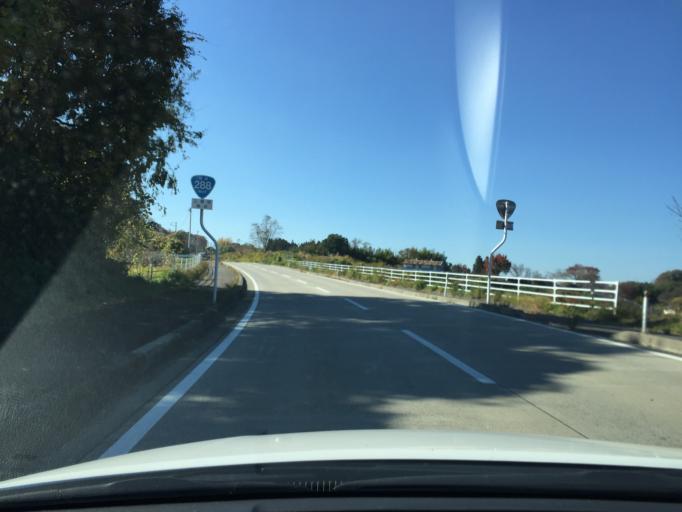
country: JP
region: Fukushima
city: Miharu
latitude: 37.4467
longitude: 140.5178
